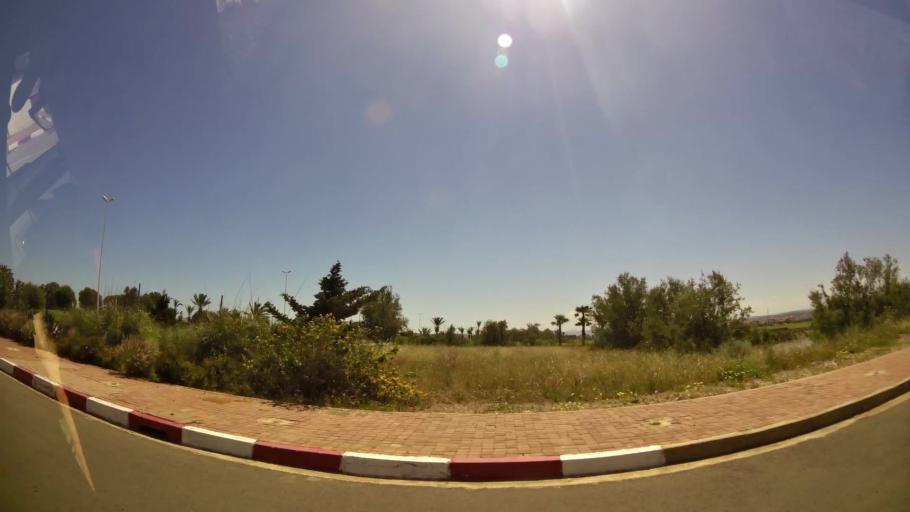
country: MA
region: Oriental
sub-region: Berkane-Taourirt
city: Madagh
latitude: 35.1080
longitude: -2.3114
